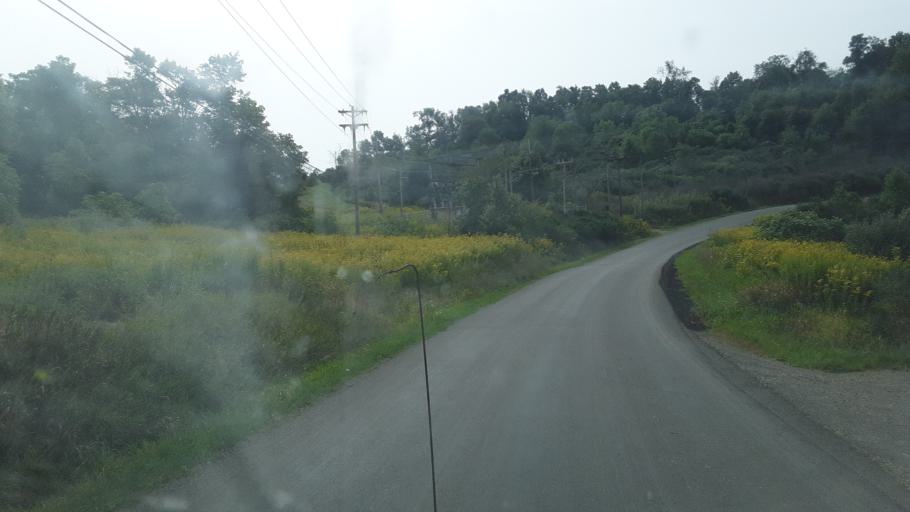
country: US
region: Pennsylvania
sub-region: Jefferson County
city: Punxsutawney
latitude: 40.9487
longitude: -79.1267
